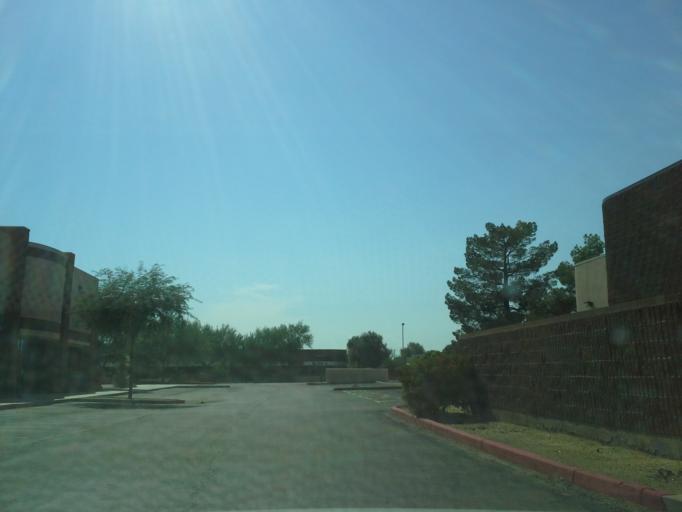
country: US
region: Arizona
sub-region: Maricopa County
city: Paradise Valley
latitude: 33.6172
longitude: -111.9030
